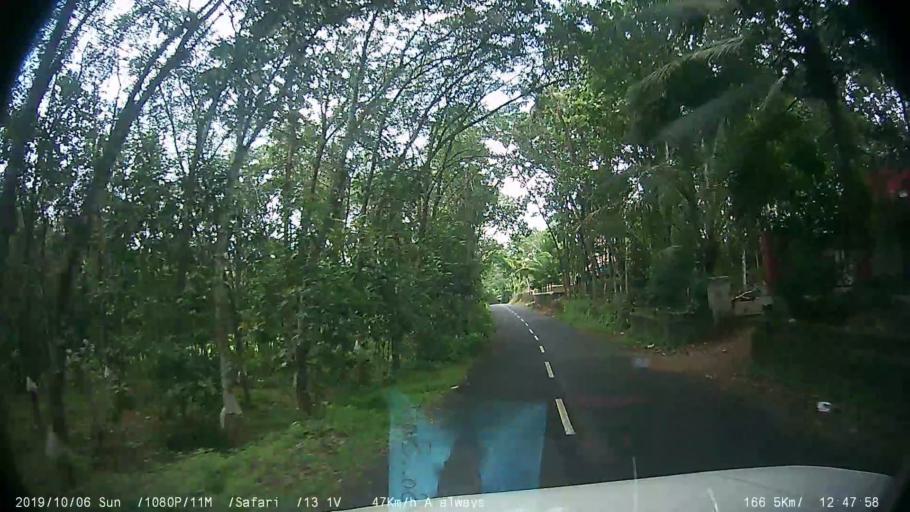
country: IN
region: Kerala
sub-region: Kottayam
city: Palackattumala
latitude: 9.7771
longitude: 76.5993
